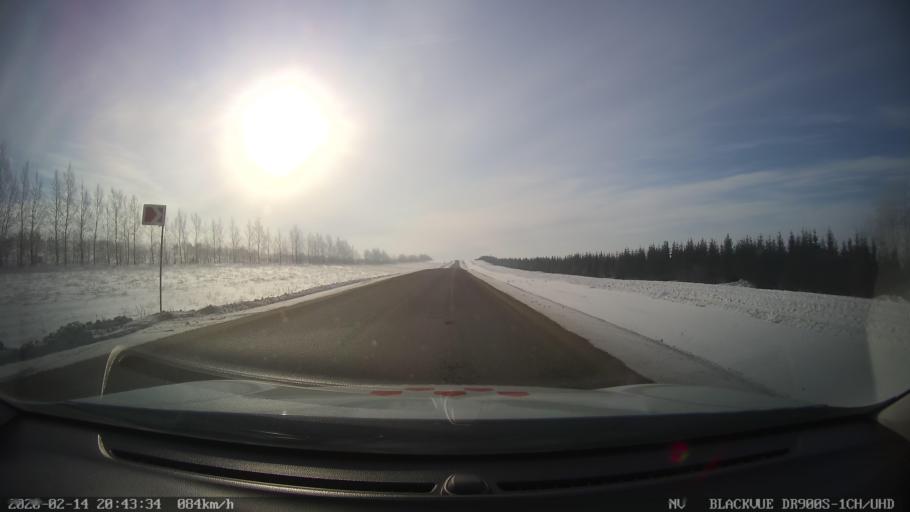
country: RU
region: Tatarstan
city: Kuybyshevskiy Zaton
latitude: 55.3065
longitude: 49.1484
